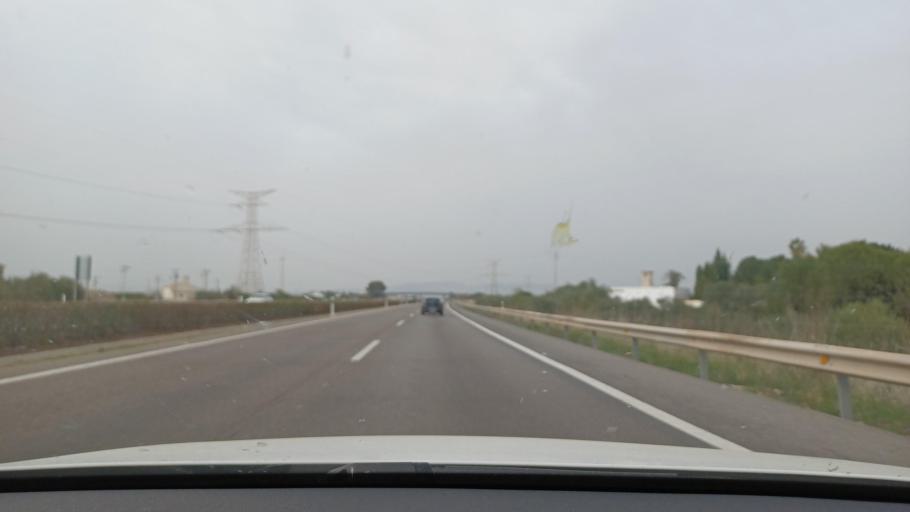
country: ES
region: Valencia
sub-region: Provincia de Castello
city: Vila-real
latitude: 39.9299
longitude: -0.1352
